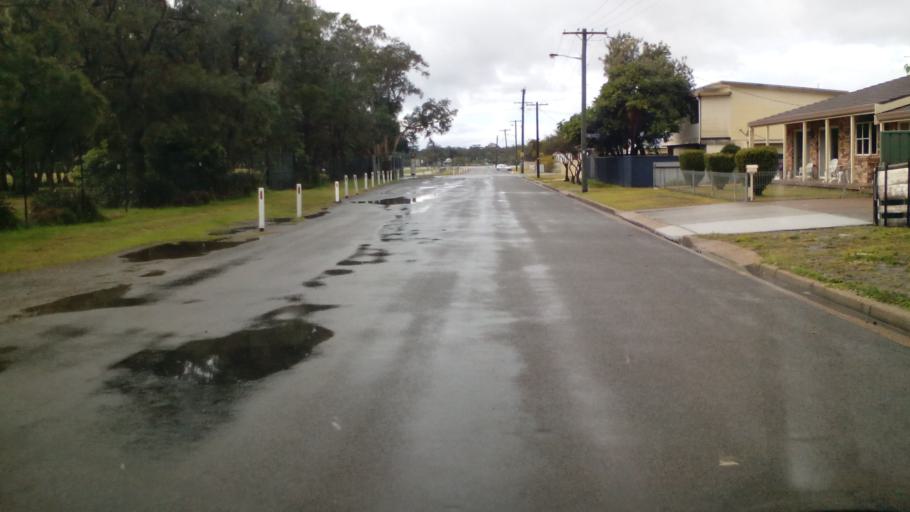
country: AU
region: New South Wales
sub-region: Lake Macquarie Shire
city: Belmont South
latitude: -33.0757
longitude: 151.6349
